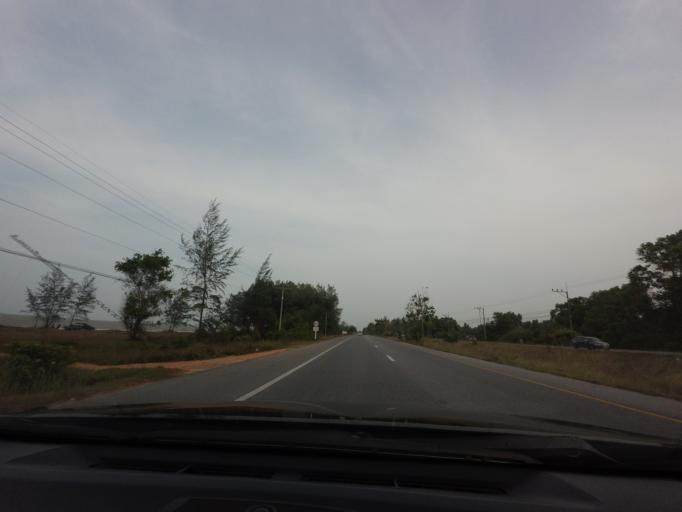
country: TH
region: Songkhla
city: Thepha
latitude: 6.9346
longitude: 100.8776
